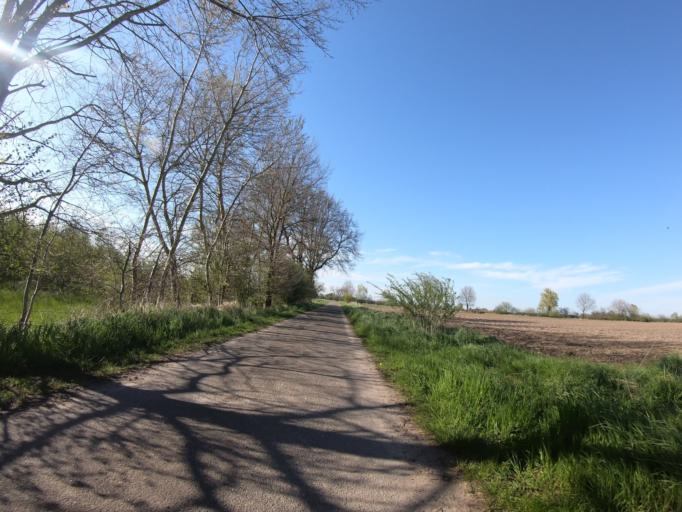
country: DE
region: Lower Saxony
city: Rotgesbuttel
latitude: 52.4054
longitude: 10.5326
